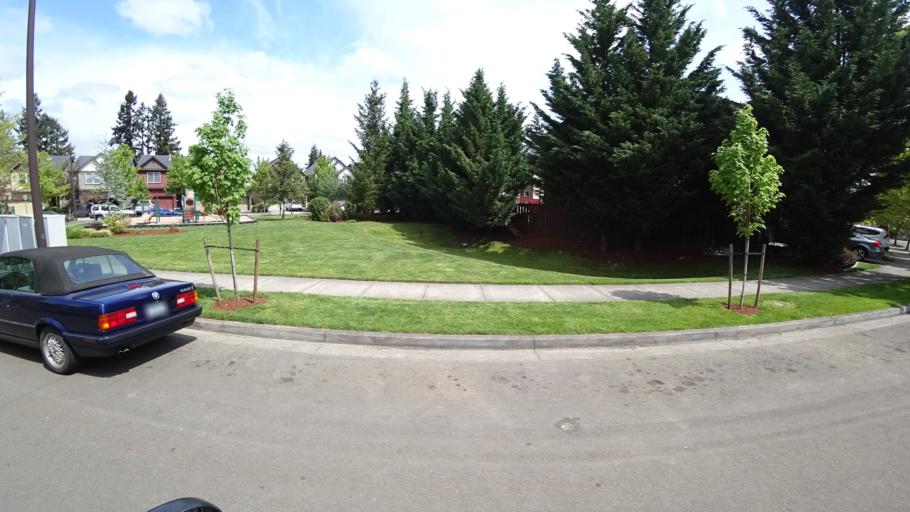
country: US
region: Oregon
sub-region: Washington County
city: Hillsboro
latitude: 45.5398
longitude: -122.9977
